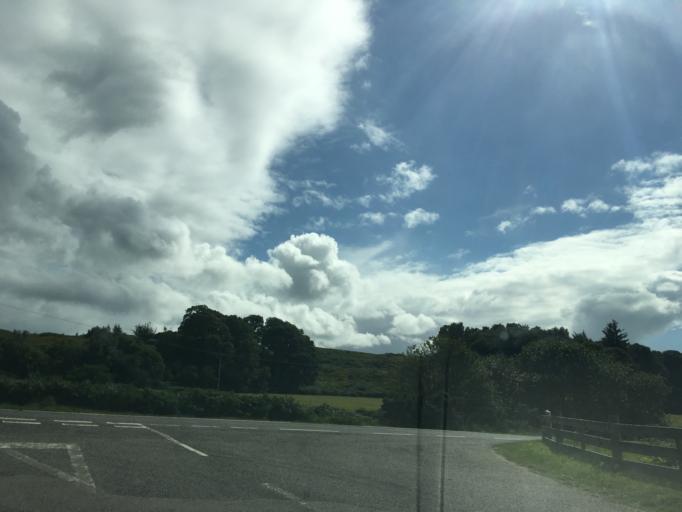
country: GB
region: Scotland
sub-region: Argyll and Bute
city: Oban
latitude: 56.4508
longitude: -5.4065
